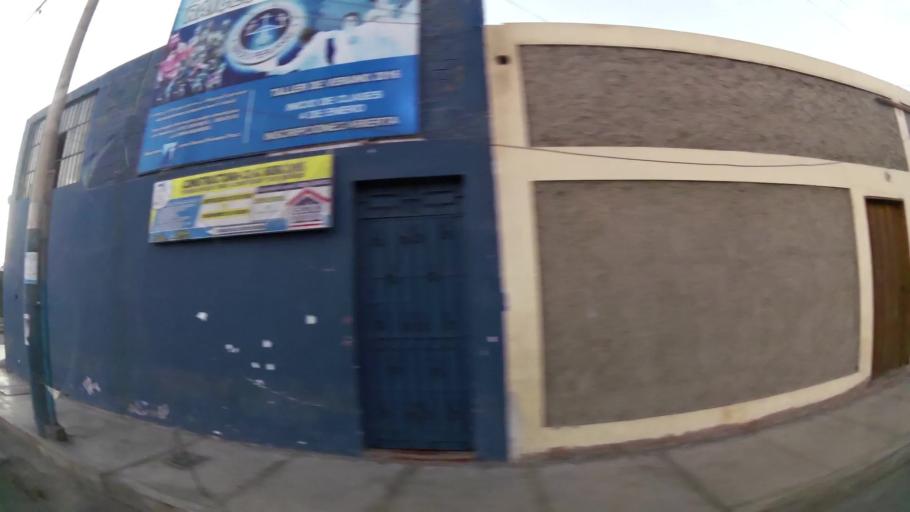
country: PE
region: Ica
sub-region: Provincia de Pisco
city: Pisco
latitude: -13.7071
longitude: -76.2044
